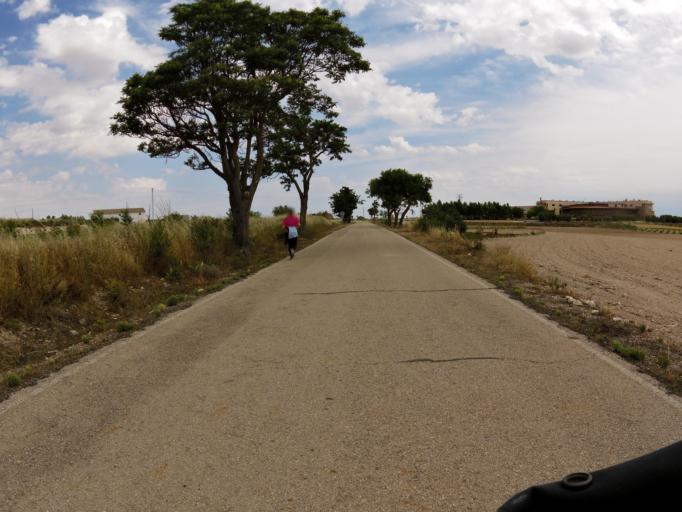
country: ES
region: Castille-La Mancha
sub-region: Provincia de Albacete
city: Valdeganga
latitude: 39.1260
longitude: -1.6814
